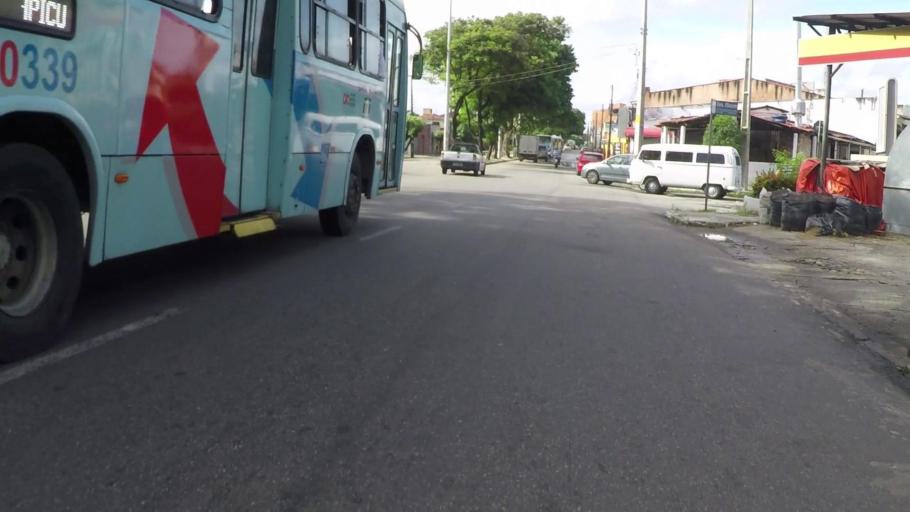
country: BR
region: Ceara
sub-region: Fortaleza
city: Fortaleza
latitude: -3.7104
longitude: -38.5899
